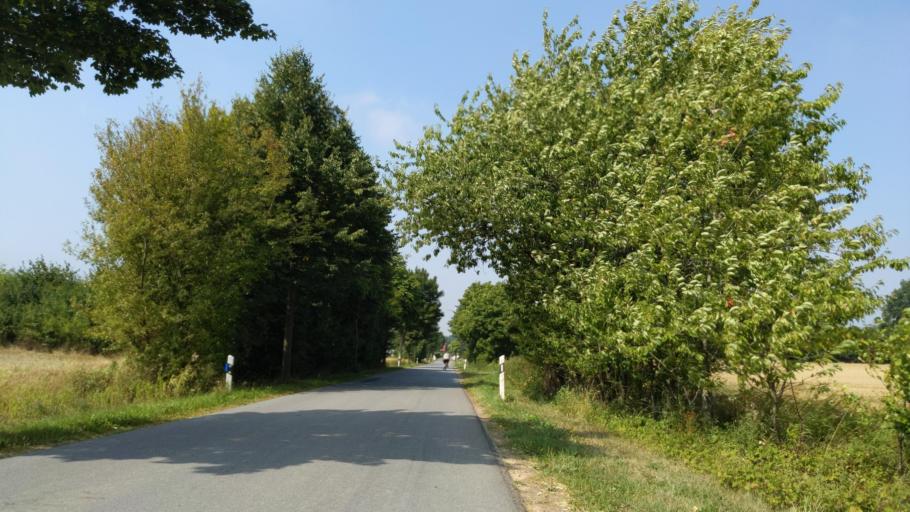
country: DE
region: Schleswig-Holstein
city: Monkhagen
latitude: 53.9217
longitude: 10.5810
